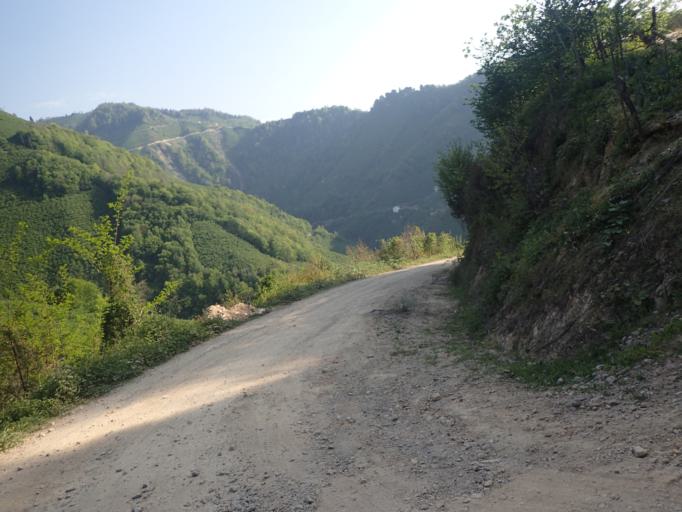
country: TR
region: Ordu
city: Kabaduz
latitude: 40.7914
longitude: 37.8895
